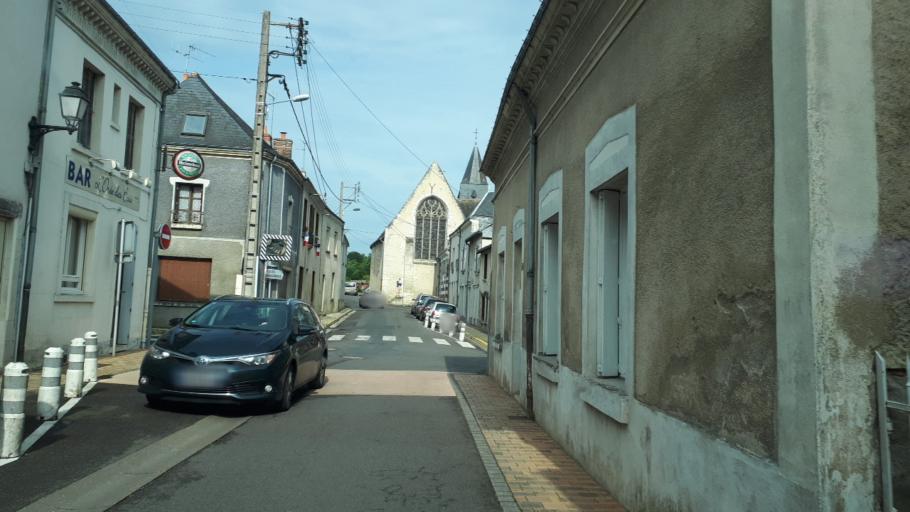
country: FR
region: Centre
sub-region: Departement d'Indre-et-Loire
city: Monnaie
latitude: 47.5017
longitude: 0.7841
